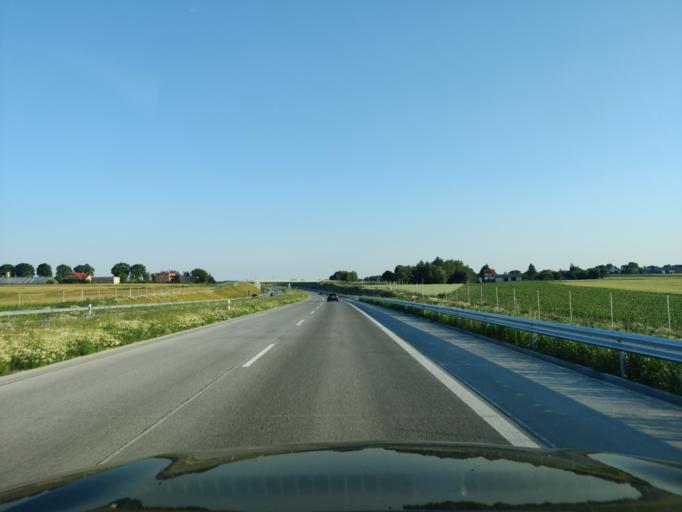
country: PL
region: Masovian Voivodeship
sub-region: Powiat mlawski
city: Mlawa
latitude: 53.1192
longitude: 20.4100
